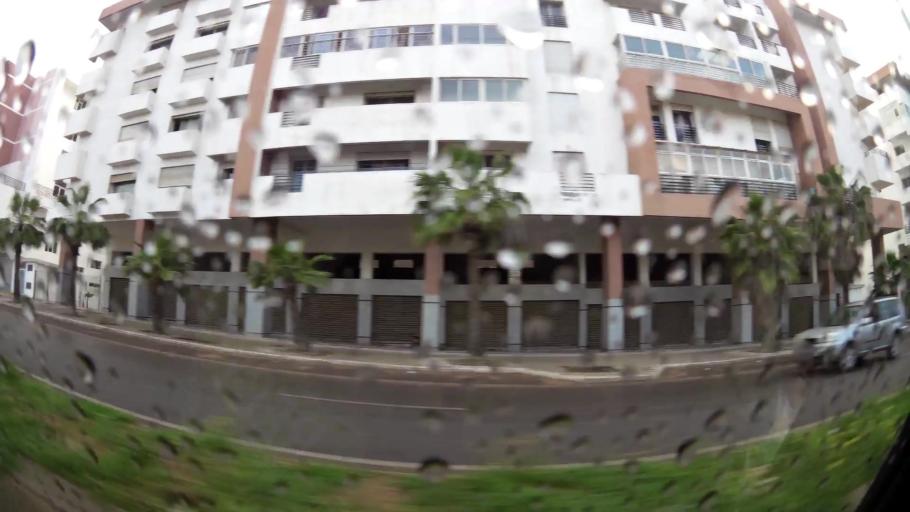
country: MA
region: Doukkala-Abda
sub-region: El-Jadida
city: El Jadida
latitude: 33.2321
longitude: -8.4933
